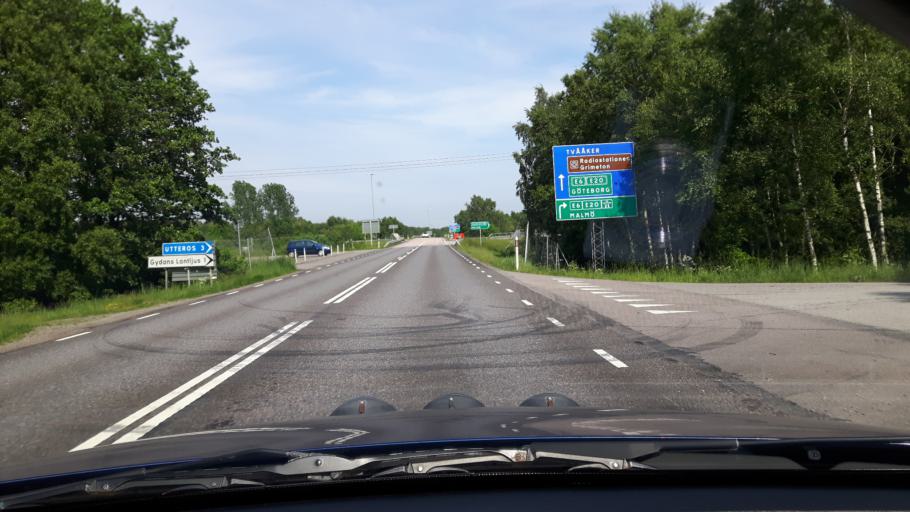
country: SE
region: Halland
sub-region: Varbergs Kommun
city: Tvaaker
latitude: 57.0481
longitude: 12.3614
